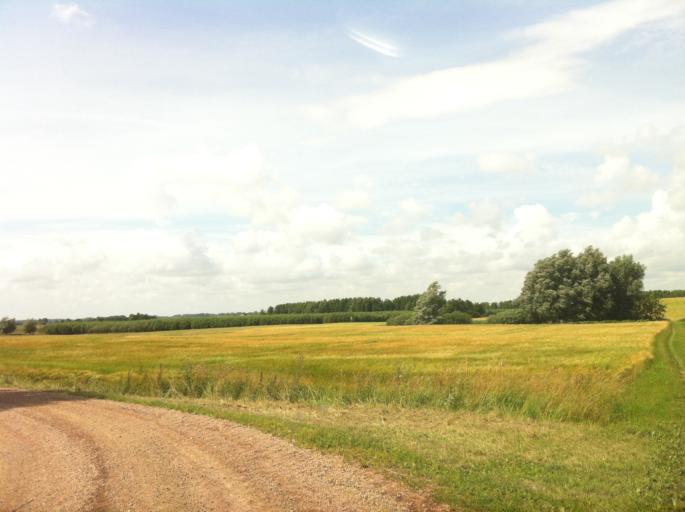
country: SE
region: Skane
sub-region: Skurups Kommun
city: Skurup
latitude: 55.4455
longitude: 13.4378
